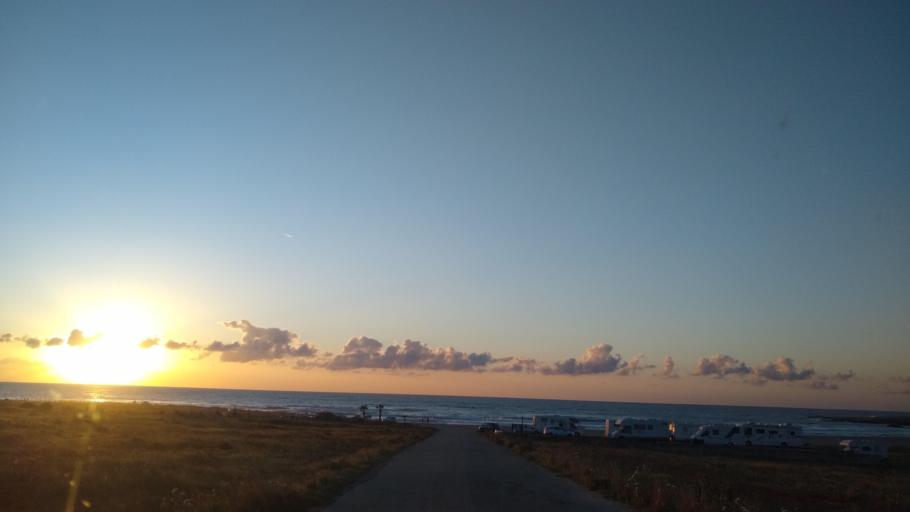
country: IT
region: Sicily
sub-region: Trapani
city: Castelluzzo
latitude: 38.1232
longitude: 12.7300
